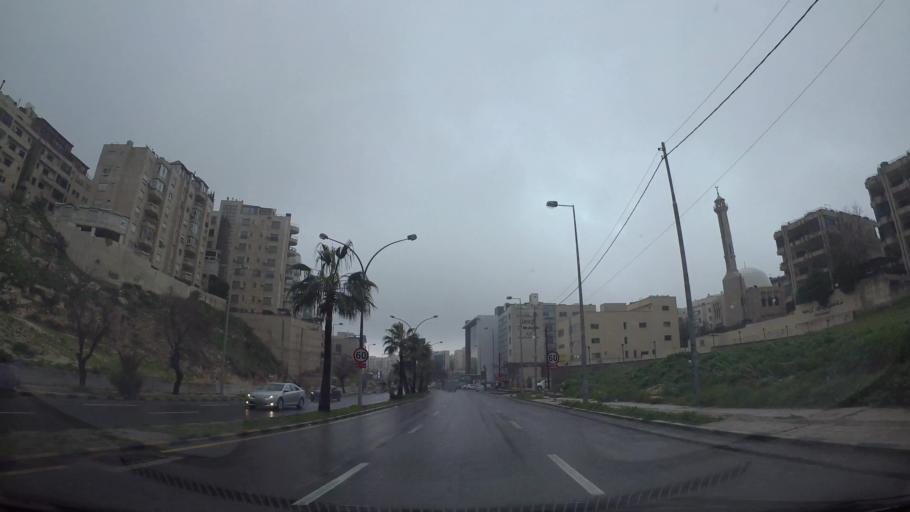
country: JO
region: Amman
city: Amman
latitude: 31.9634
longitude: 35.8888
